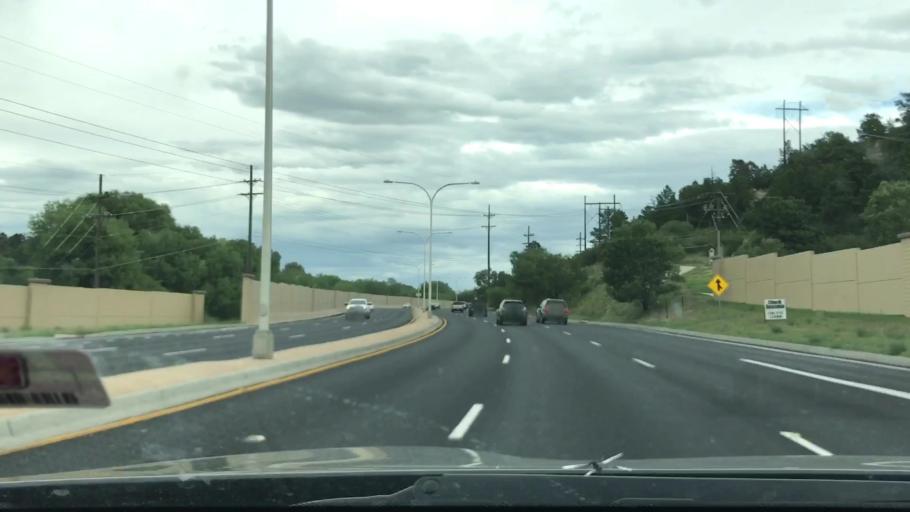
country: US
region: Colorado
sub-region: El Paso County
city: Colorado Springs
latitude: 38.8891
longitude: -104.7826
